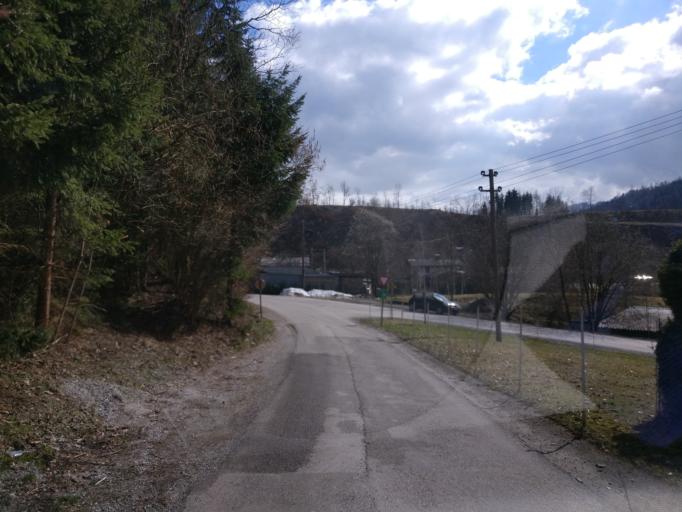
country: AT
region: Salzburg
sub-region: Politischer Bezirk Sankt Johann im Pongau
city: Bischofshofen
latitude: 47.4379
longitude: 13.2158
